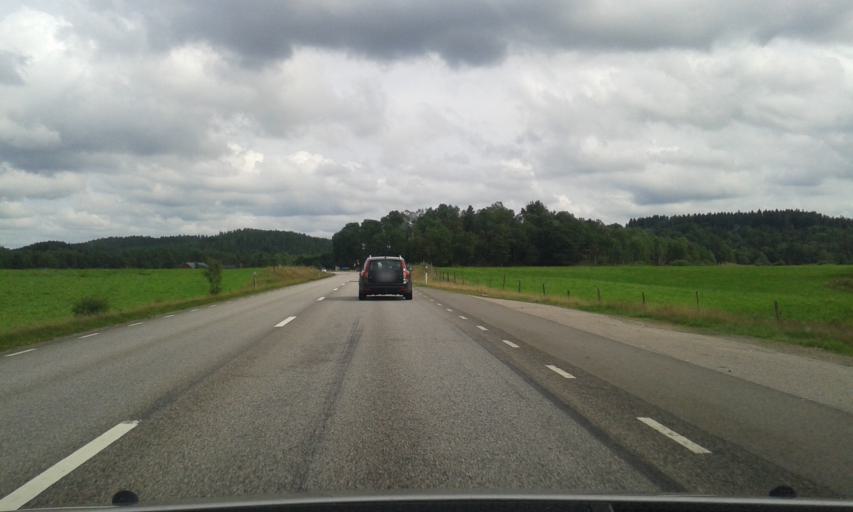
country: SE
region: Vaestra Goetaland
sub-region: Marks Kommun
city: Horred
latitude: 57.1518
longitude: 12.6782
